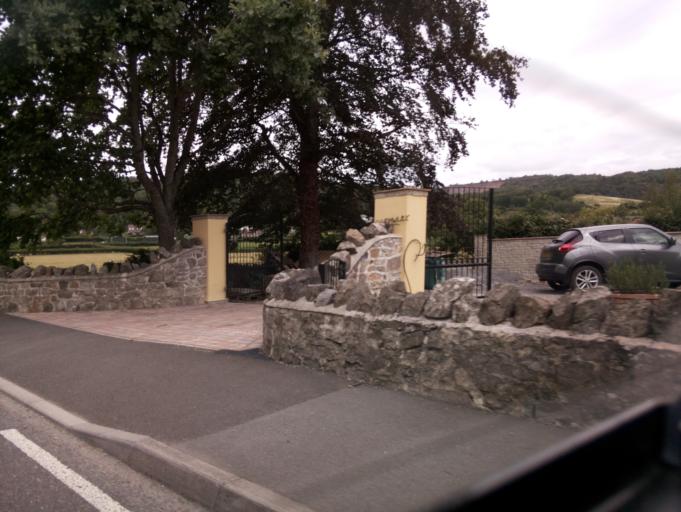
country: GB
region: England
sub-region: Somerset
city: Cheddar
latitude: 51.2828
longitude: -2.7895
